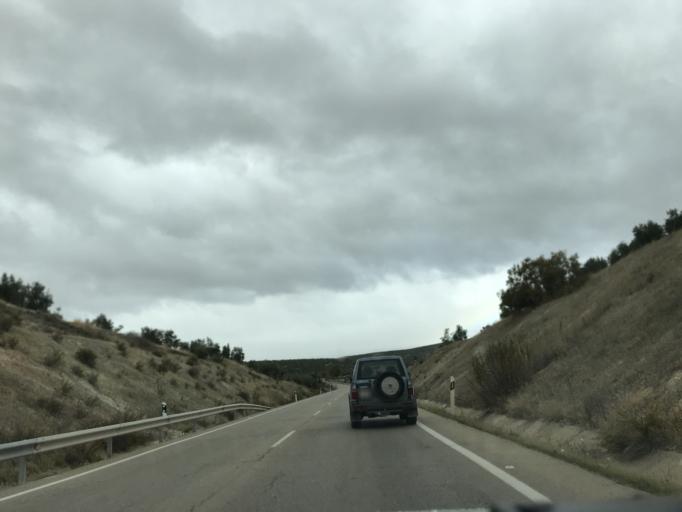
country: ES
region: Andalusia
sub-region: Provincia de Jaen
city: Peal de Becerro
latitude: 37.9234
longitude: -3.1352
